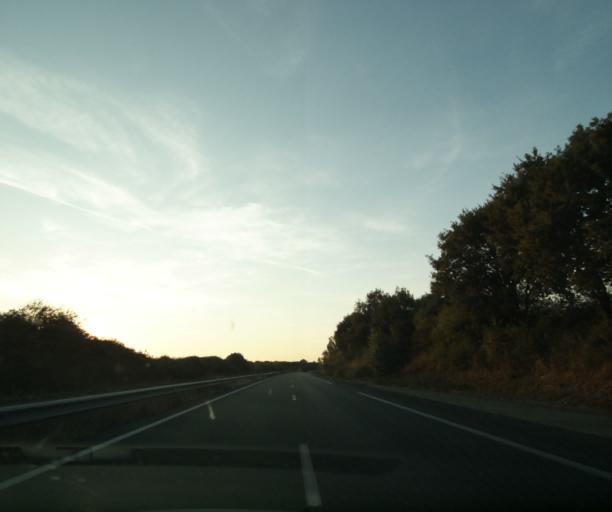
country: FR
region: Aquitaine
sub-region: Departement du Lot-et-Garonne
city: Fourques-sur-Garonne
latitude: 44.3809
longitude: 0.2108
